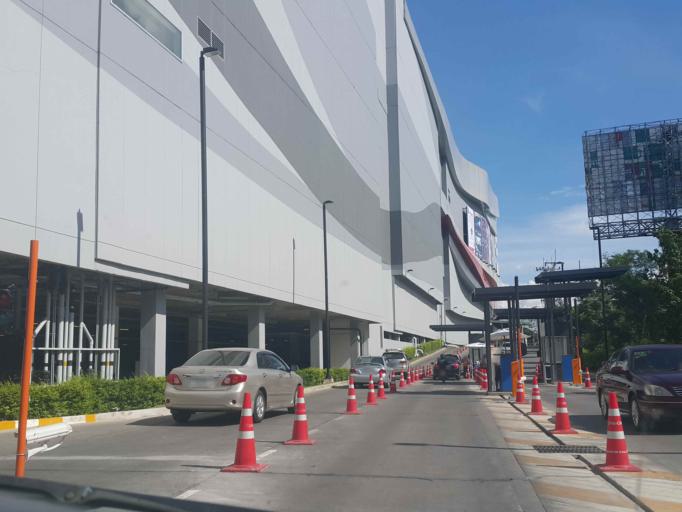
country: TH
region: Chiang Mai
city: Chiang Mai
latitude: 18.8080
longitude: 99.0175
